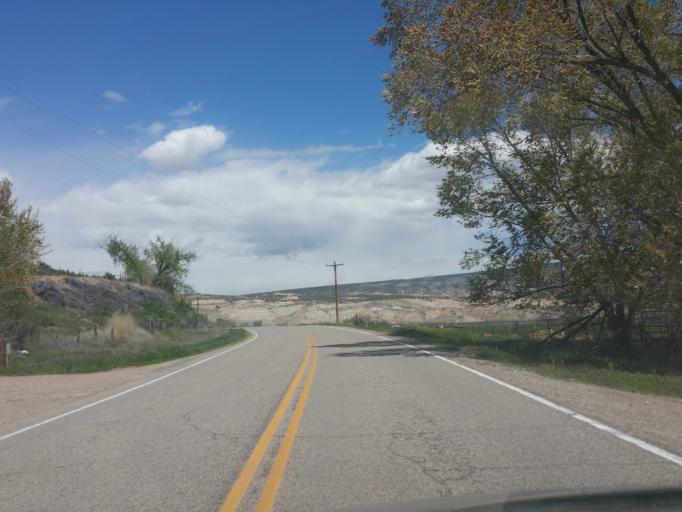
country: US
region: Utah
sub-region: Uintah County
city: Naples
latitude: 40.4091
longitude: -109.3399
